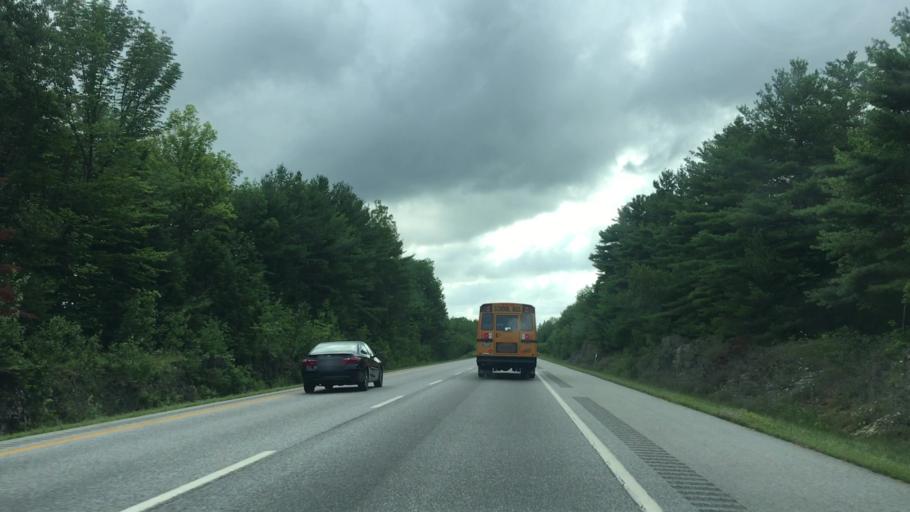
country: US
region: Maine
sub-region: Penobscot County
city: Plymouth
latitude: 44.7894
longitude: -69.1768
